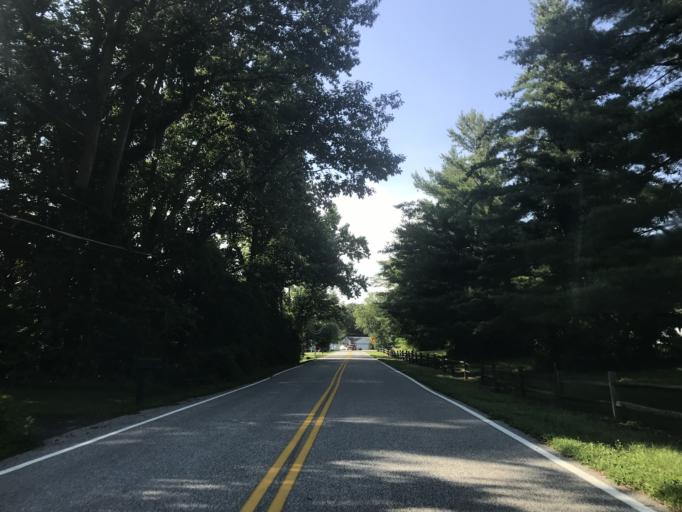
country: US
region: Maryland
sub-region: Harford County
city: Aberdeen
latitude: 39.5097
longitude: -76.1294
